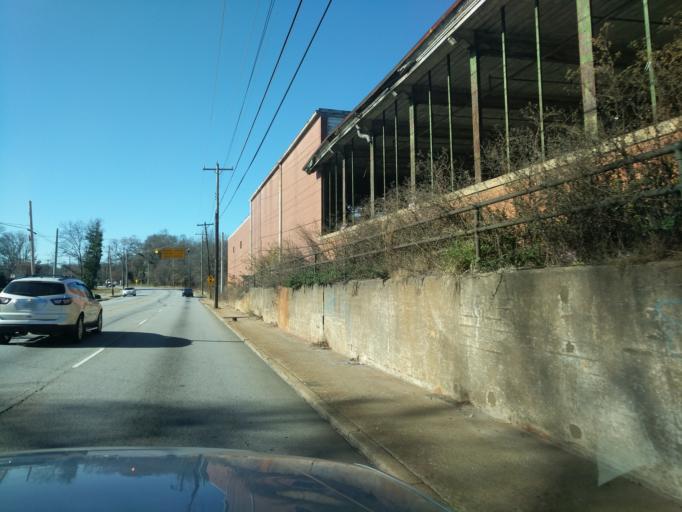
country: US
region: South Carolina
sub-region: Greenville County
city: Judson
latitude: 34.8439
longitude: -82.4220
